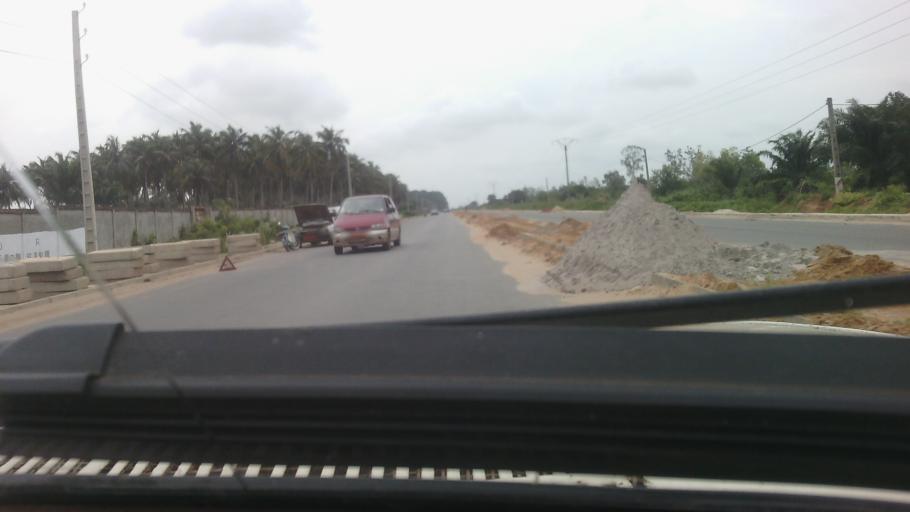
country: BJ
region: Atlantique
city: Ouidah
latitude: 6.3676
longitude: 2.1272
